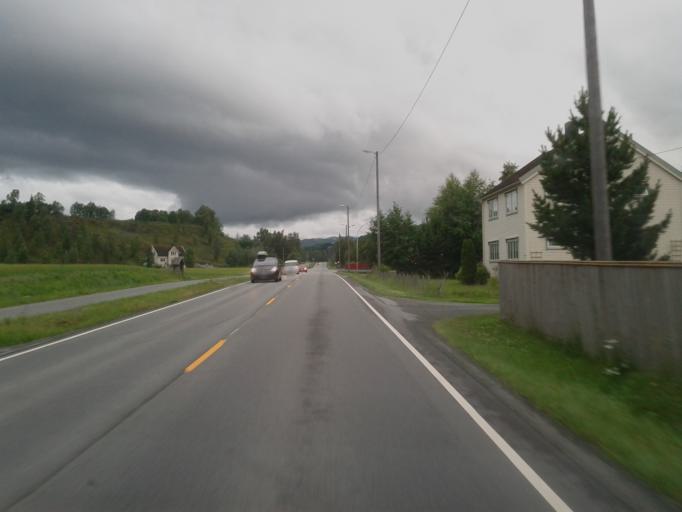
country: NO
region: Sor-Trondelag
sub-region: Melhus
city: Lundamo
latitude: 63.1428
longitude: 10.2612
